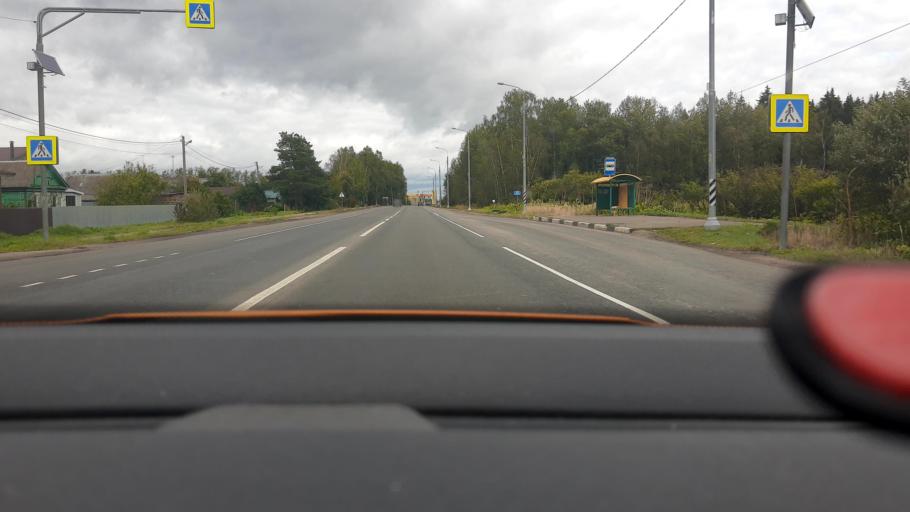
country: RU
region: Moskovskaya
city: Krasnoarmeysk
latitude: 56.0737
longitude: 38.0368
